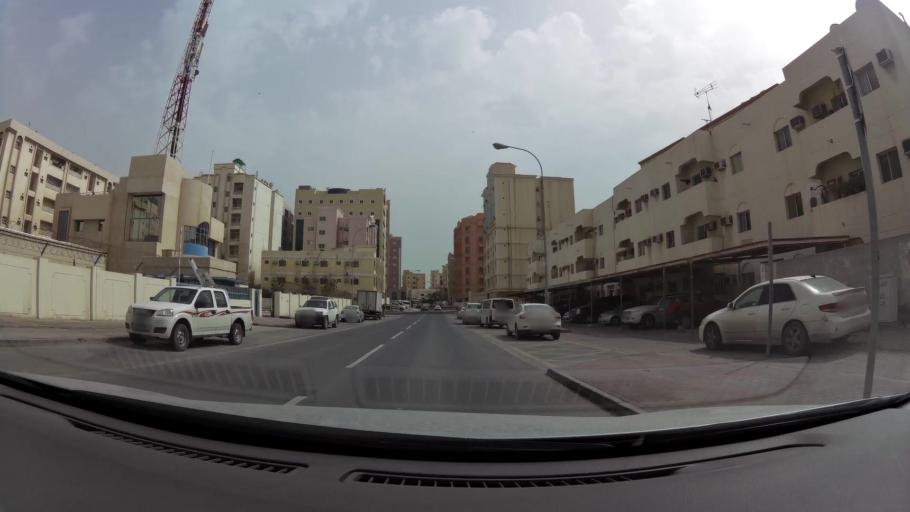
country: QA
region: Baladiyat ad Dawhah
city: Doha
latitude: 25.2663
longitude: 51.5431
